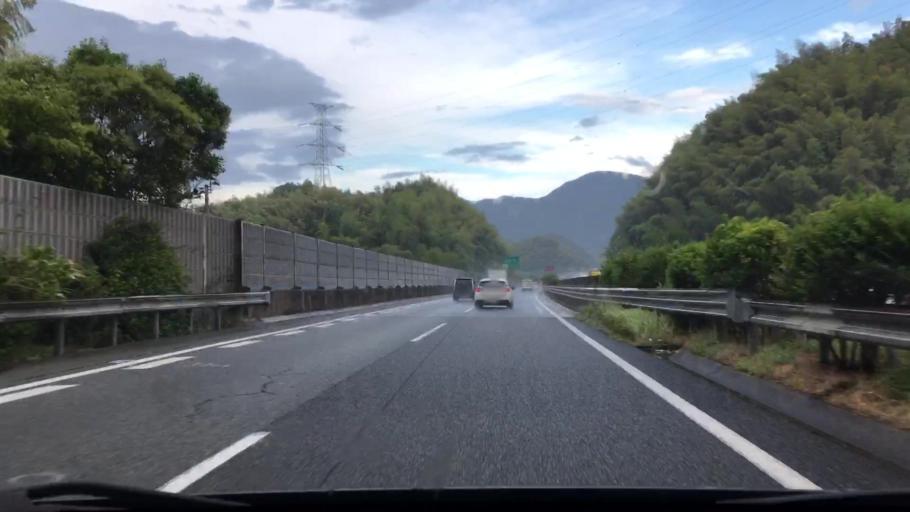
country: JP
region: Fukuoka
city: Kitakyushu
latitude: 33.8075
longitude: 130.8434
